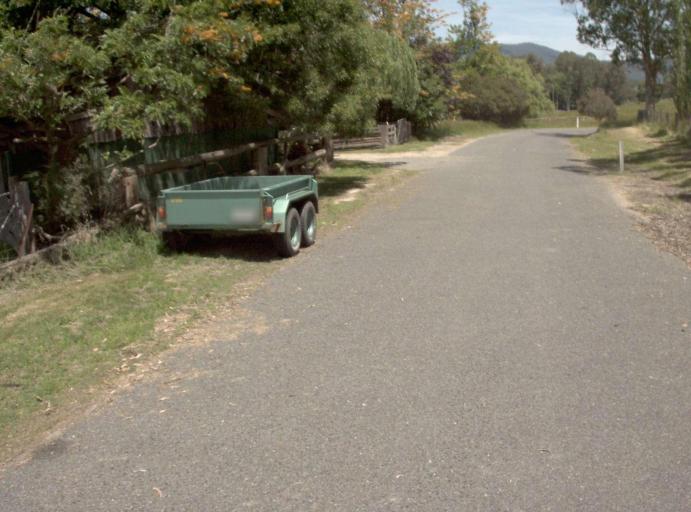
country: AU
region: New South Wales
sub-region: Bombala
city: Bombala
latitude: -37.3824
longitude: 149.0133
